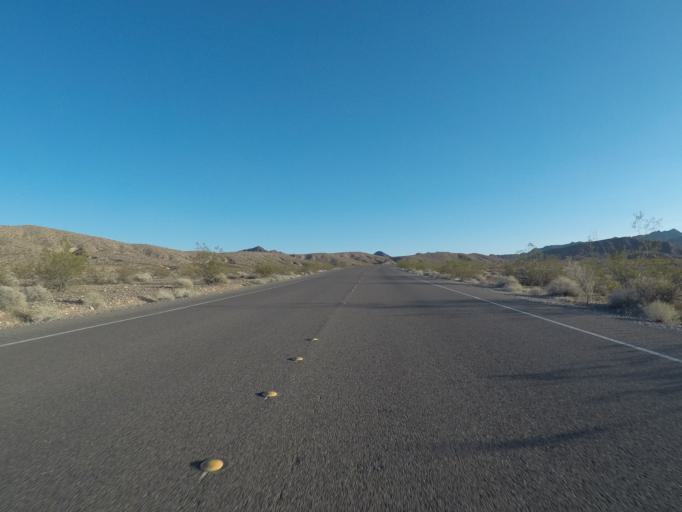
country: US
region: Nevada
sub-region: Clark County
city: Moapa Valley
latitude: 36.2822
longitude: -114.4892
